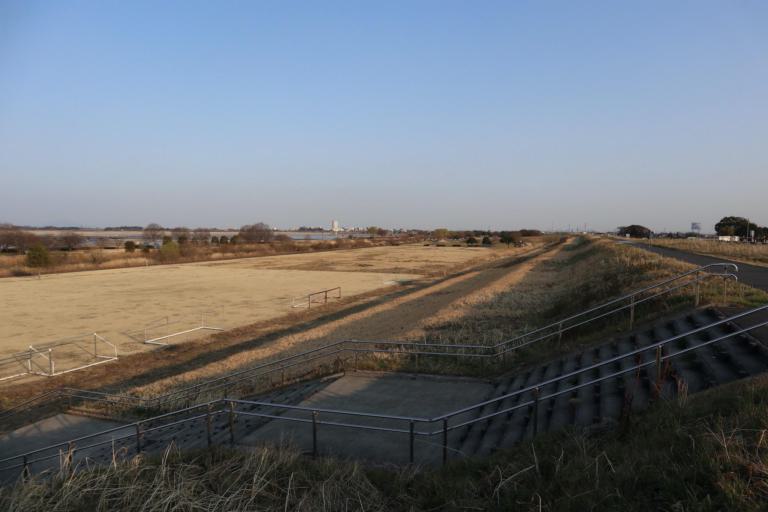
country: JP
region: Tochigi
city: Fujioka
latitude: 36.2118
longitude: 139.6625
